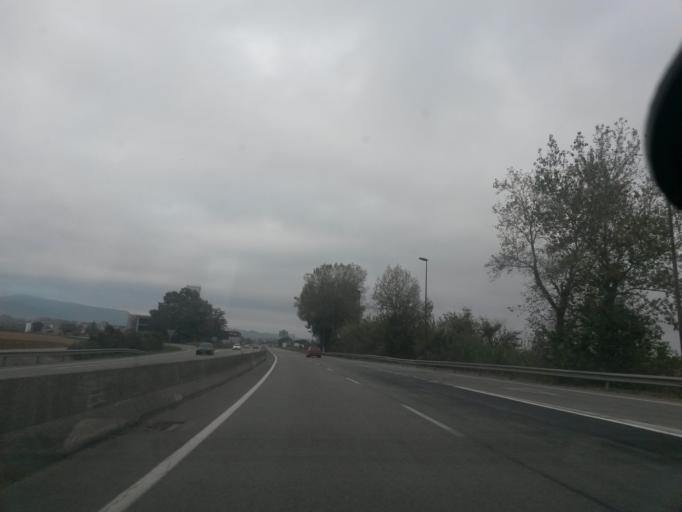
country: ES
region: Catalonia
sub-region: Provincia de Girona
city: Cornella del Terri
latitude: 42.0904
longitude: 2.8086
